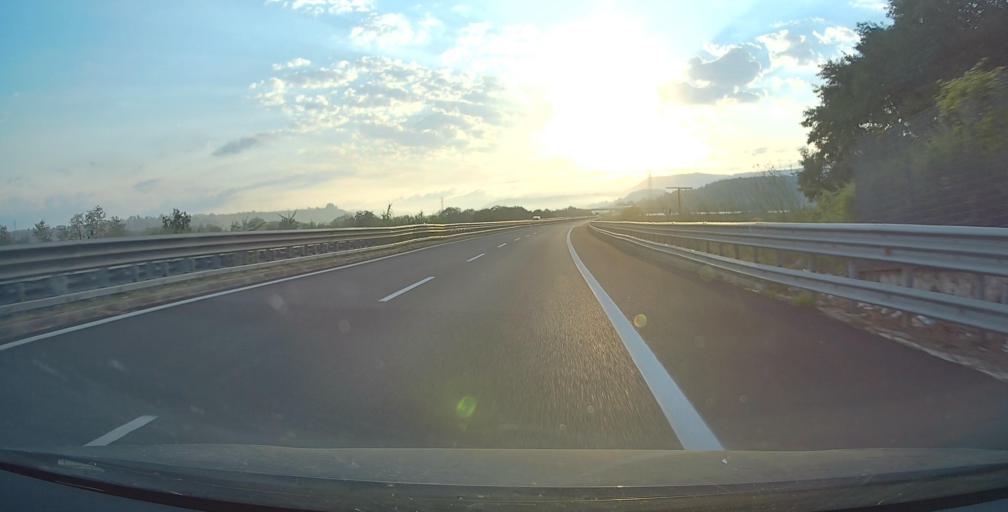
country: IT
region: Calabria
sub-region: Provincia di Reggio Calabria
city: Rosarno
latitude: 38.4991
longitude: 16.0206
